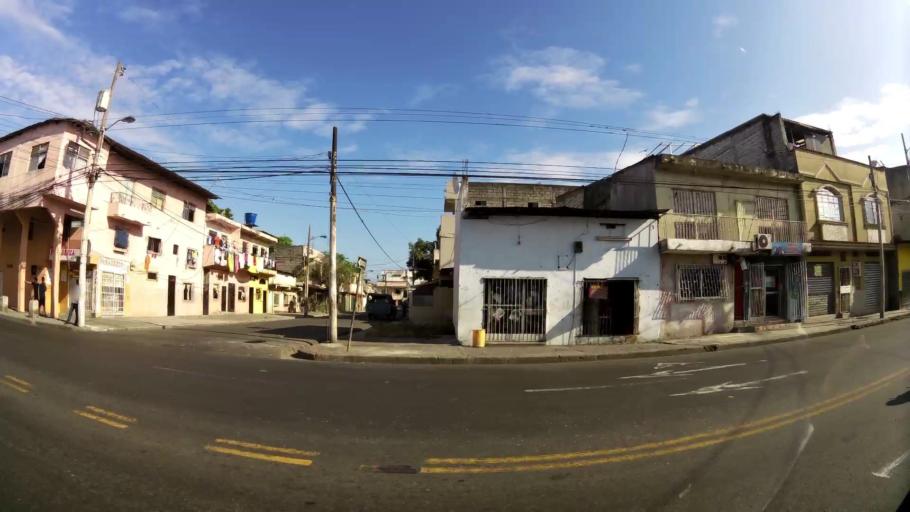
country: EC
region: Guayas
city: Guayaquil
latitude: -2.2041
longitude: -79.9201
